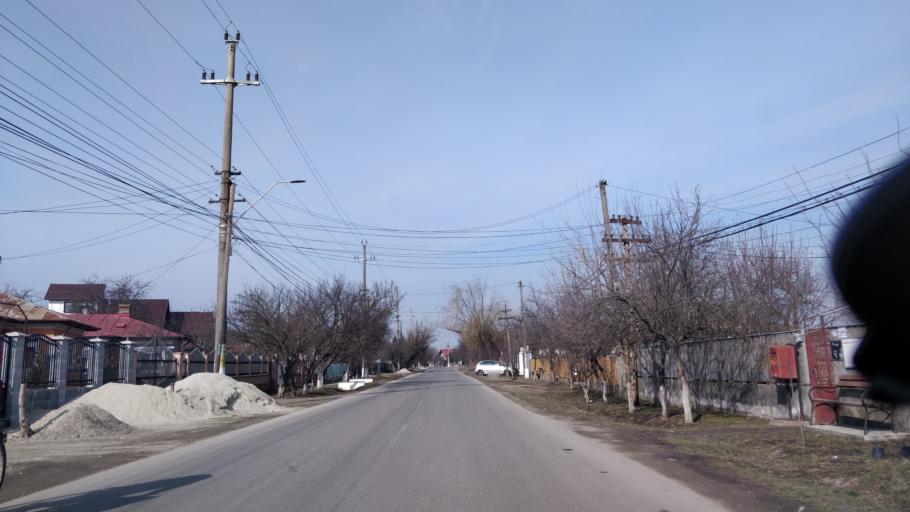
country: RO
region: Giurgiu
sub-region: Comuna Ulmi
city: Ulmi
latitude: 44.4734
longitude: 25.7660
